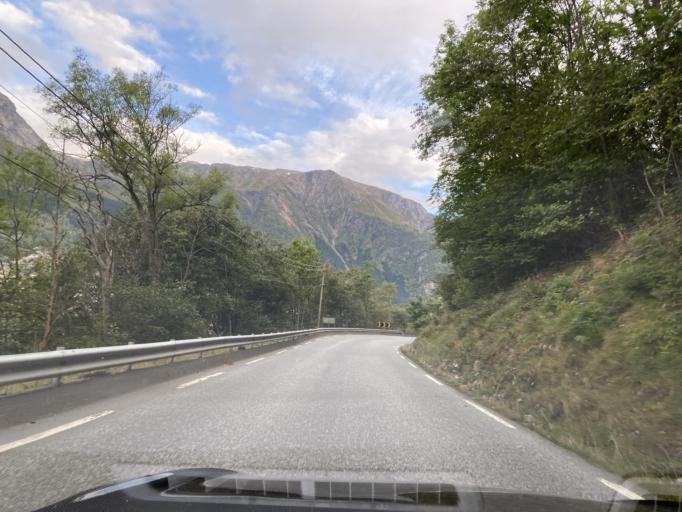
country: NO
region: Hordaland
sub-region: Odda
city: Odda
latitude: 60.0845
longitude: 6.5512
